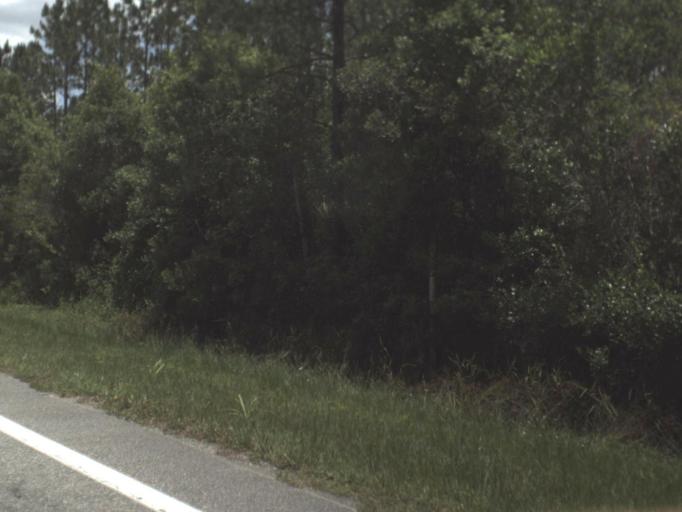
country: US
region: Florida
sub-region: Levy County
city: Bronson
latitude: 29.4130
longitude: -82.6822
